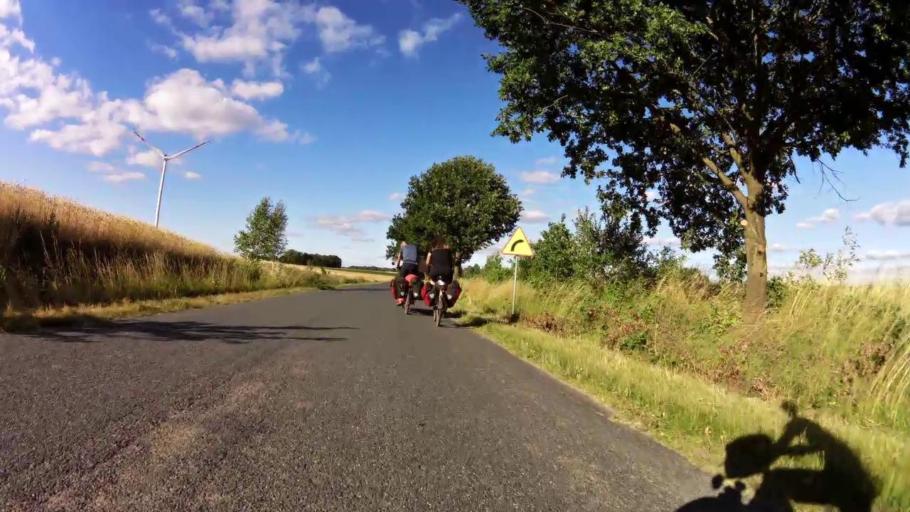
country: PL
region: West Pomeranian Voivodeship
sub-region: Powiat swidwinski
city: Swidwin
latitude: 53.6885
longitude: 15.7621
